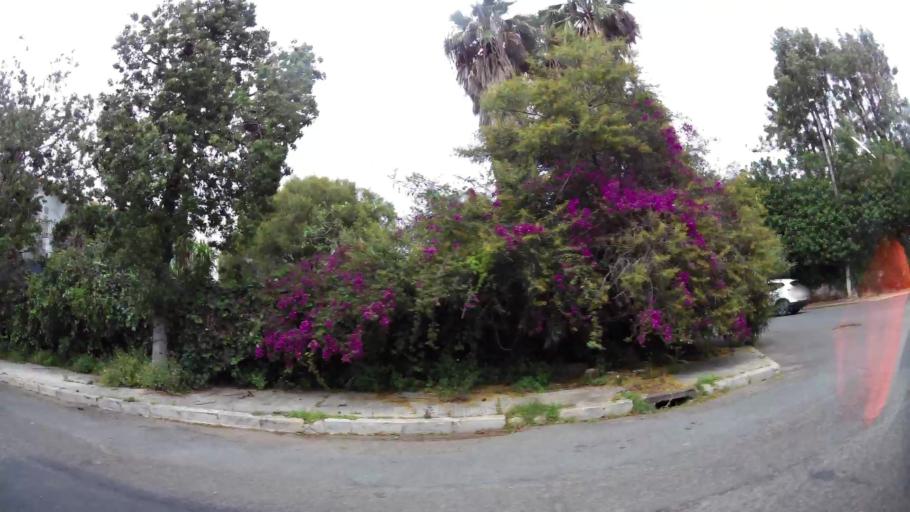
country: MA
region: Grand Casablanca
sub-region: Casablanca
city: Casablanca
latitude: 33.5602
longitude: -7.6359
